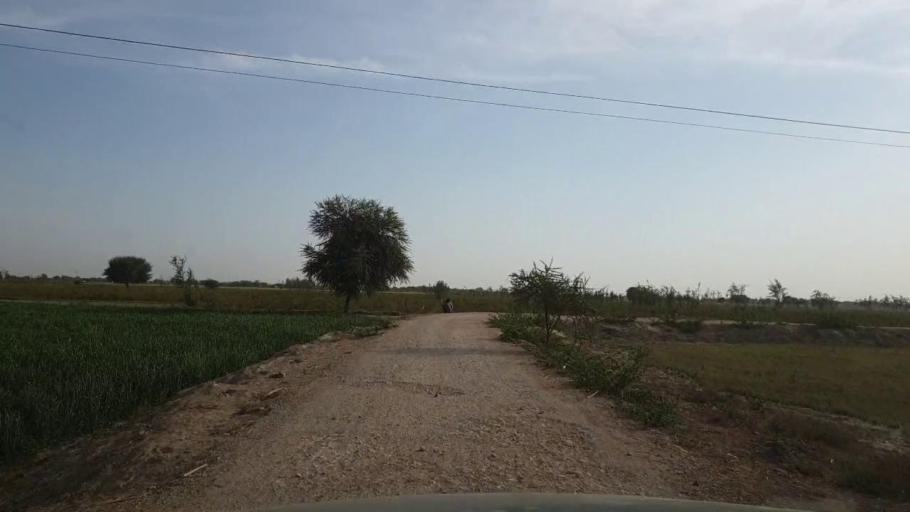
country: PK
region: Sindh
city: Kunri
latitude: 25.1463
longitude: 69.5035
